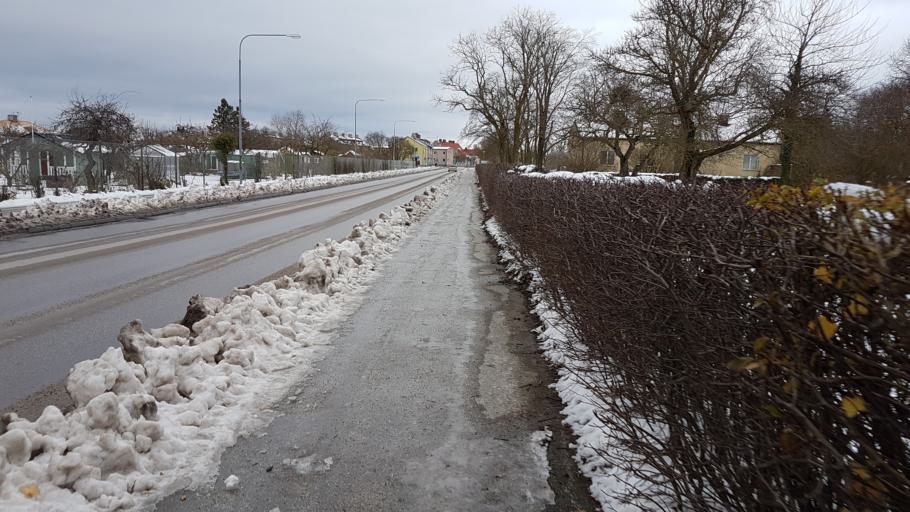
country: SE
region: Gotland
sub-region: Gotland
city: Visby
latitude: 57.6389
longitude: 18.3063
